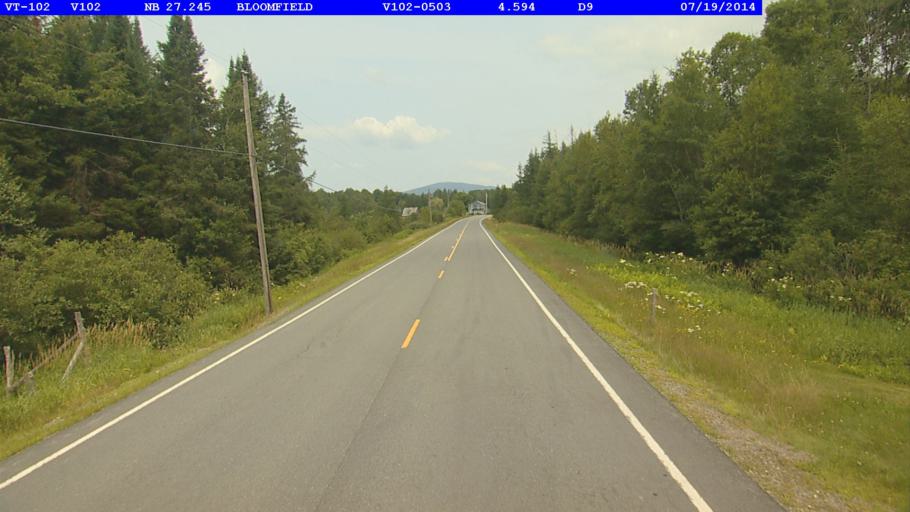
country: US
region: New Hampshire
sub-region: Coos County
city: Colebrook
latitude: 44.7971
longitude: -71.5759
